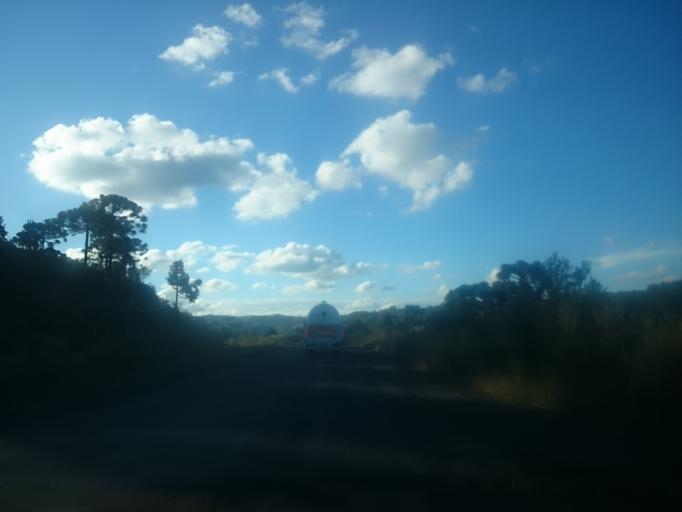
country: BR
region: Santa Catarina
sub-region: Sao Joaquim
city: Sao Joaquim
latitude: -28.0958
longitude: -50.0545
